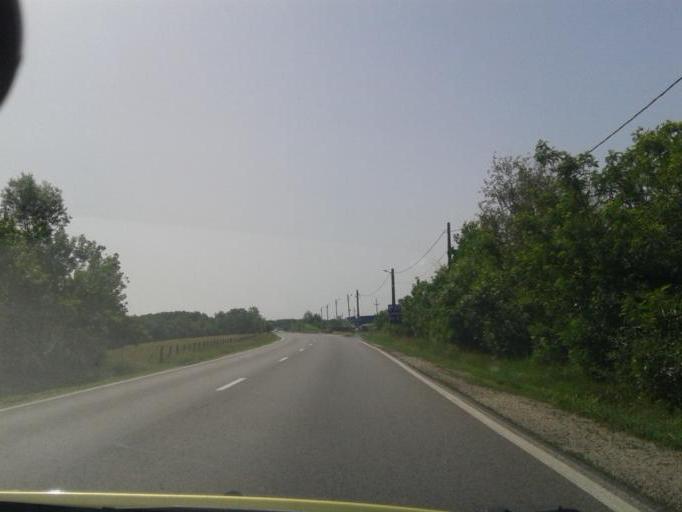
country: RO
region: Arges
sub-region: Comuna Moraresti
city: Moraresti
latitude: 45.0116
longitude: 24.5735
